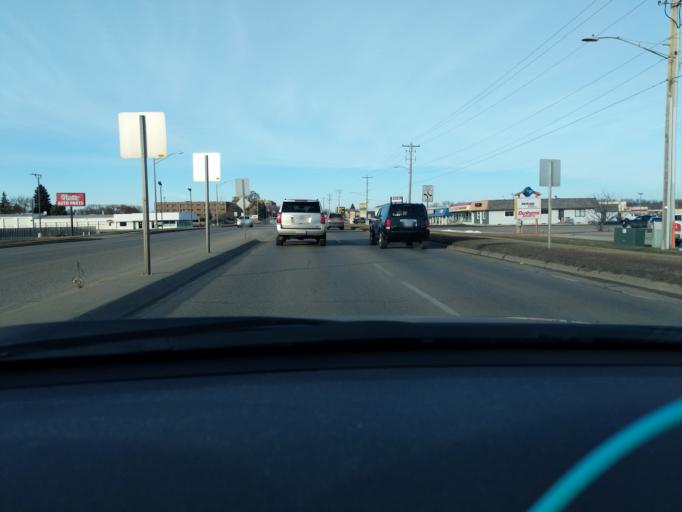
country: US
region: Minnesota
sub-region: Kandiyohi County
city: Willmar
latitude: 45.1061
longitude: -95.0427
